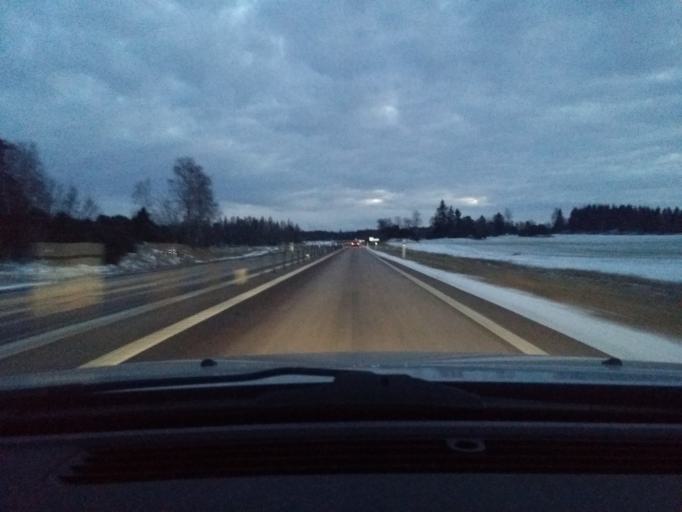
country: SE
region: Uppsala
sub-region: Enkopings Kommun
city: Orsundsbro
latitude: 59.6856
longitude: 17.2777
